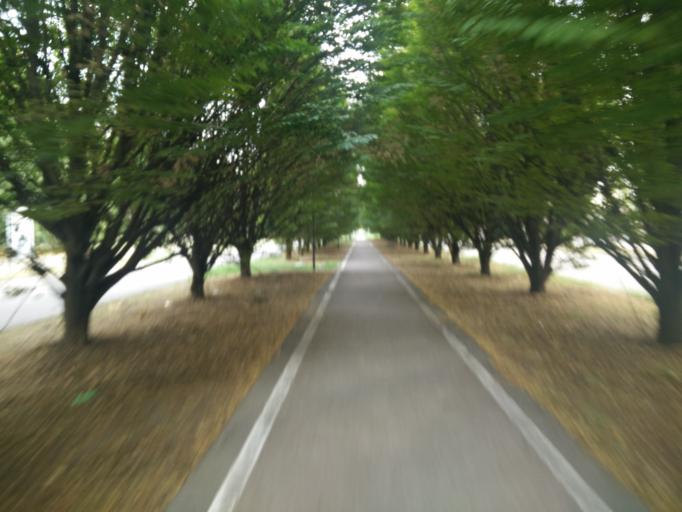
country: IT
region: Piedmont
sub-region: Provincia di Torino
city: Gerbido
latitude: 45.0345
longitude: 7.6280
